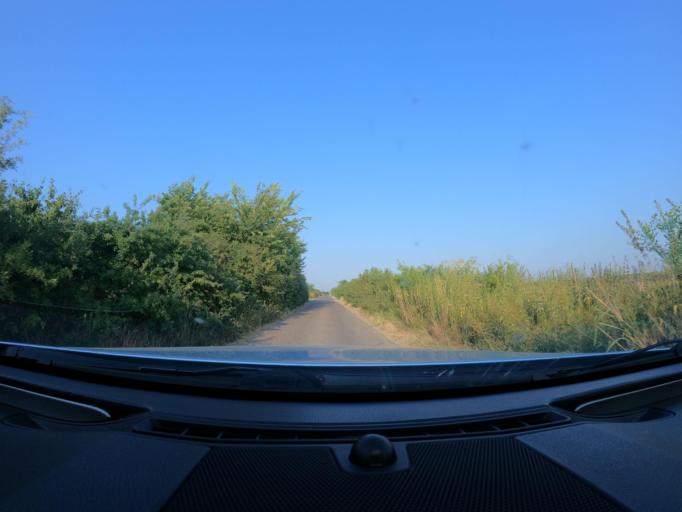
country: RS
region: Autonomna Pokrajina Vojvodina
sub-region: Sremski Okrug
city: Ruma
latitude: 45.0521
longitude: 19.7700
